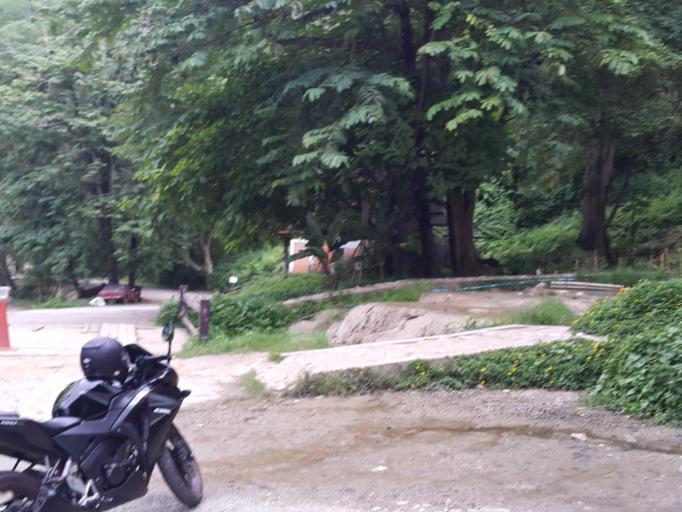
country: TH
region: Lampang
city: Wang Nuea
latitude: 19.0699
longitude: 99.7291
